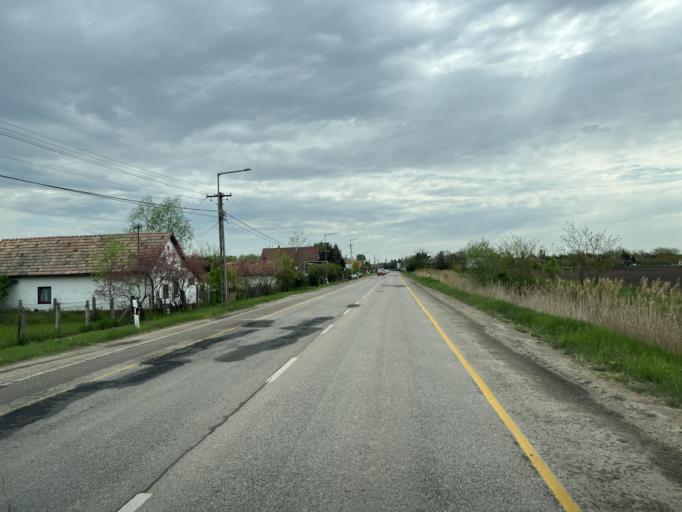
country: HU
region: Pest
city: Abony
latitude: 47.1886
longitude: 19.9842
